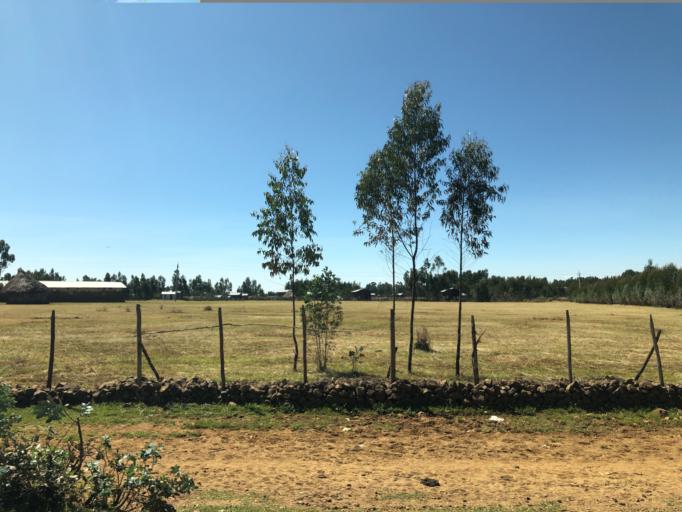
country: ET
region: Amhara
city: Lalibela
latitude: 11.6879
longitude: 38.7780
